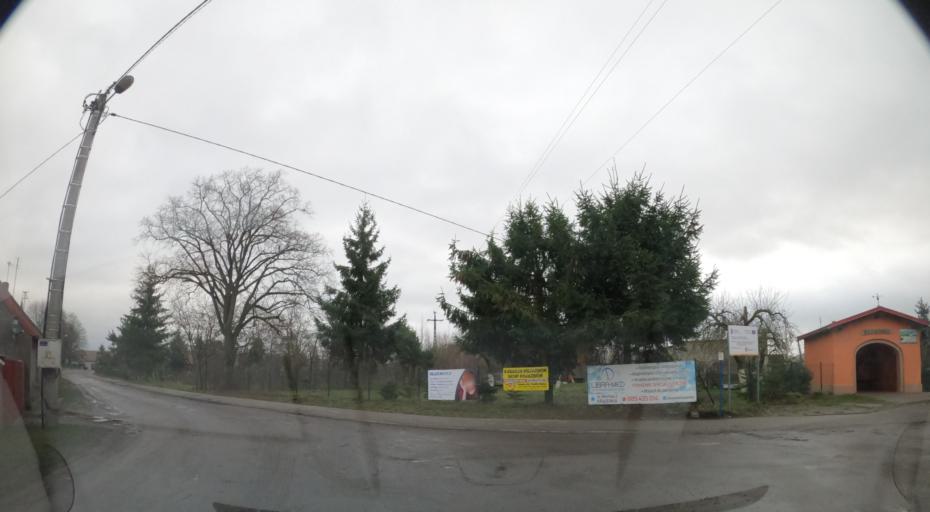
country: PL
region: Greater Poland Voivodeship
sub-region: Powiat pilski
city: Wysoka
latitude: 53.2557
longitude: 17.1197
